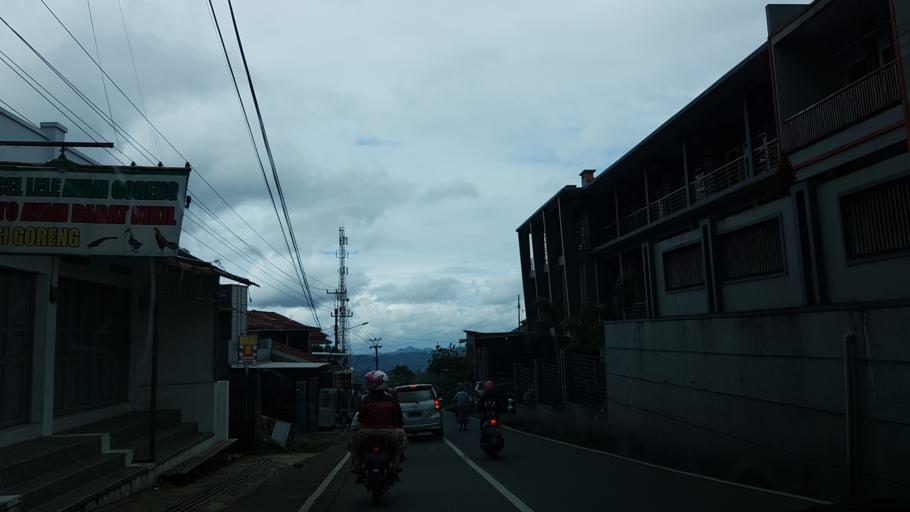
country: ID
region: West Java
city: Banjar
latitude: -7.1302
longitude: 107.4192
